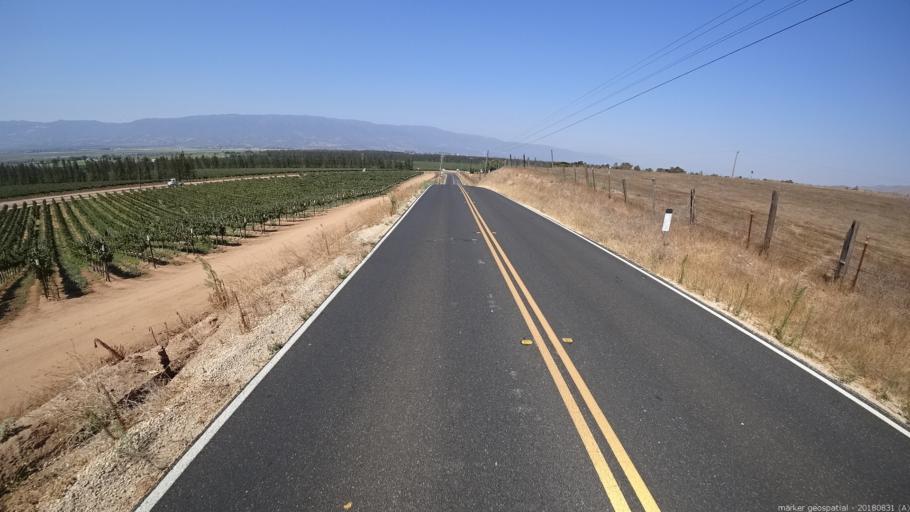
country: US
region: California
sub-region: Monterey County
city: Soledad
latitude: 36.4159
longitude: -121.2751
